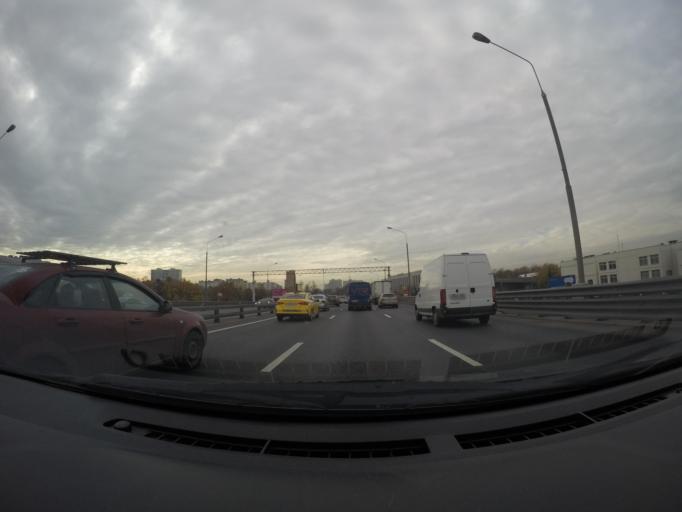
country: RU
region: Moscow
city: Vatutino
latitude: 55.8600
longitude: 37.6905
